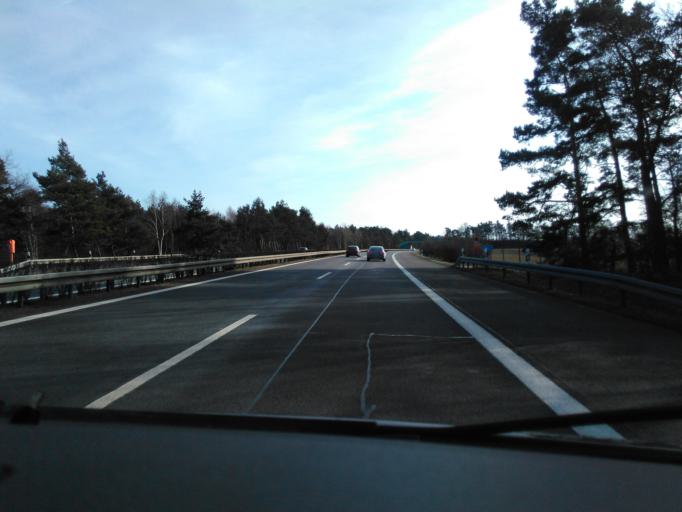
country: DE
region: Brandenburg
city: Grossraschen
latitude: 51.6088
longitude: 13.9526
